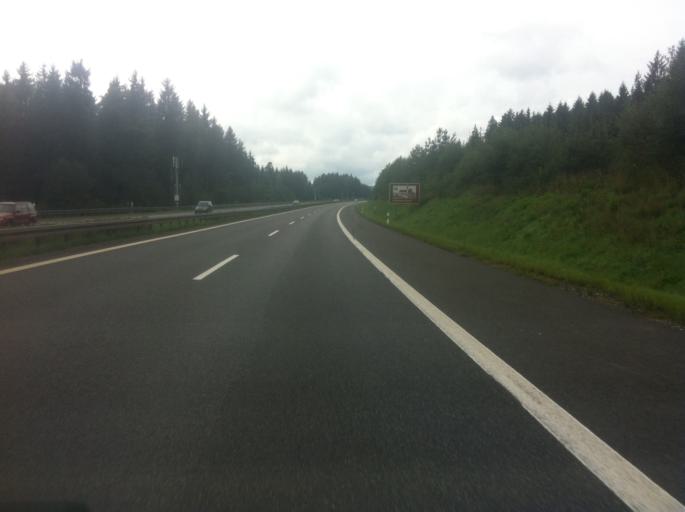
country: DE
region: Bavaria
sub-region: Upper Palatinate
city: Pleystein
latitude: 49.6300
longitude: 12.4484
